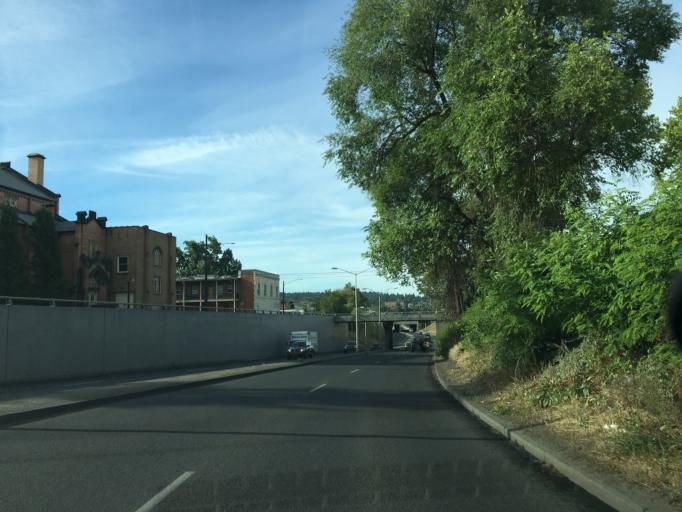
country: US
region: Washington
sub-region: Spokane County
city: Spokane
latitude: 47.6655
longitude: -117.4358
